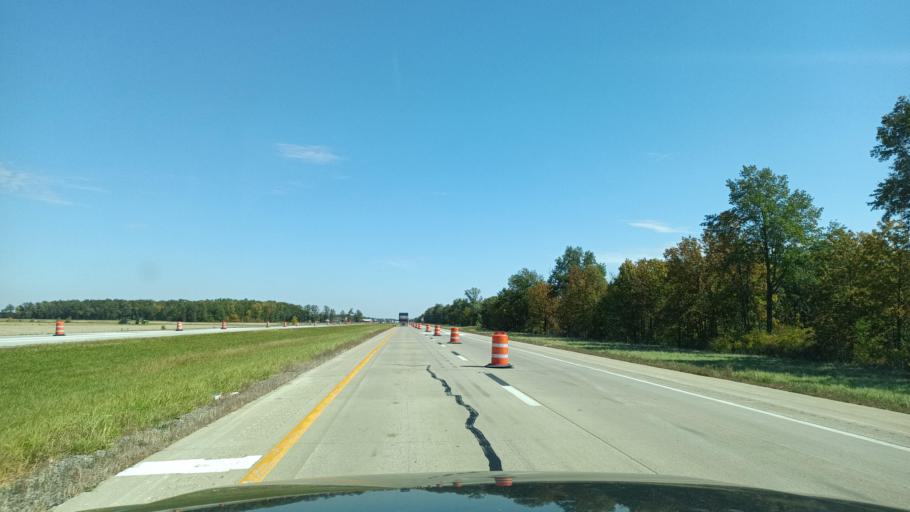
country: US
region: Ohio
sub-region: Paulding County
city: Paulding
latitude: 41.2451
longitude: -84.5002
